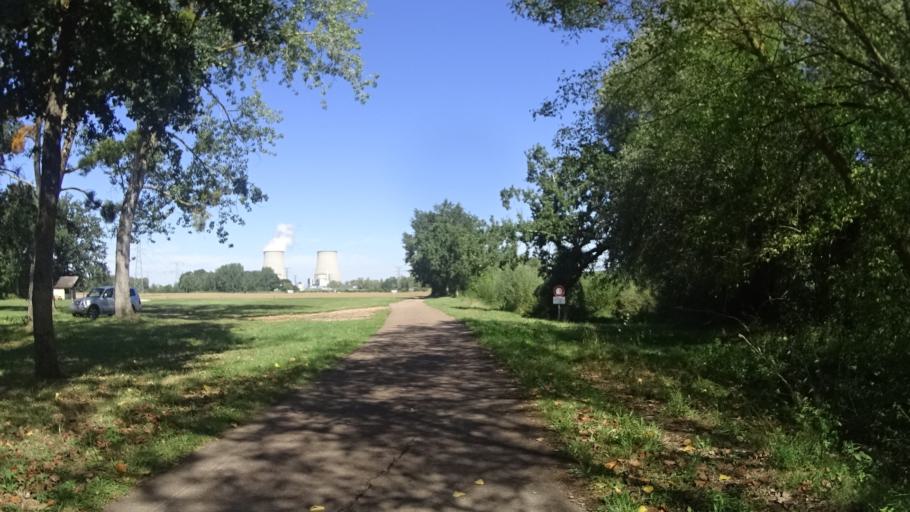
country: FR
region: Bourgogne
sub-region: Departement de la Nievre
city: Neuvy-sur-Loire
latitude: 47.4948
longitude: 2.8899
